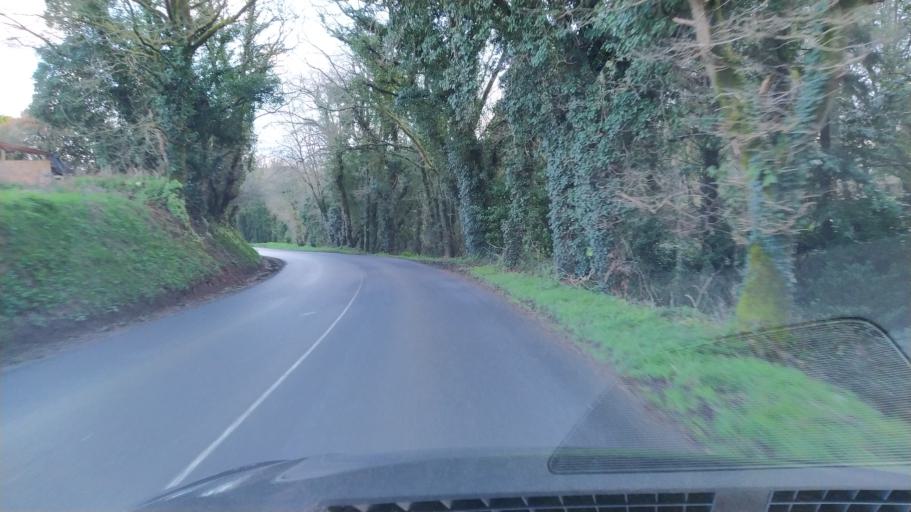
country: FR
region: Brittany
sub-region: Departement du Finistere
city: Landivisiau
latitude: 48.5019
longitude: -4.0946
